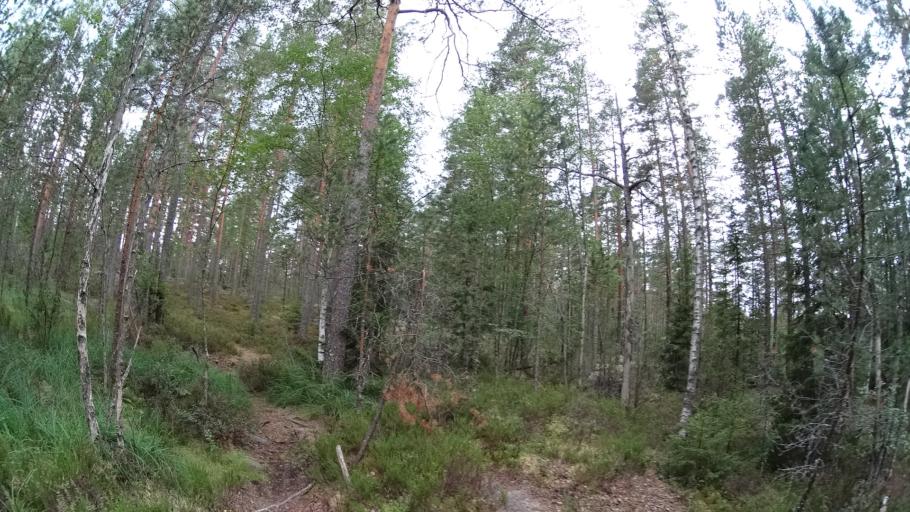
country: FI
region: Uusimaa
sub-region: Helsinki
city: Espoo
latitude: 60.3044
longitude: 24.5733
